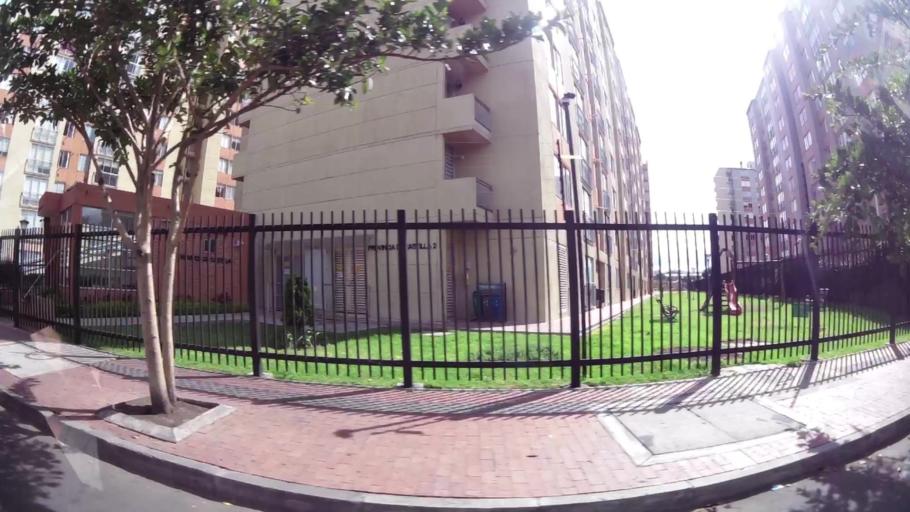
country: CO
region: Bogota D.C.
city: Bogota
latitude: 4.6459
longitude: -74.1348
